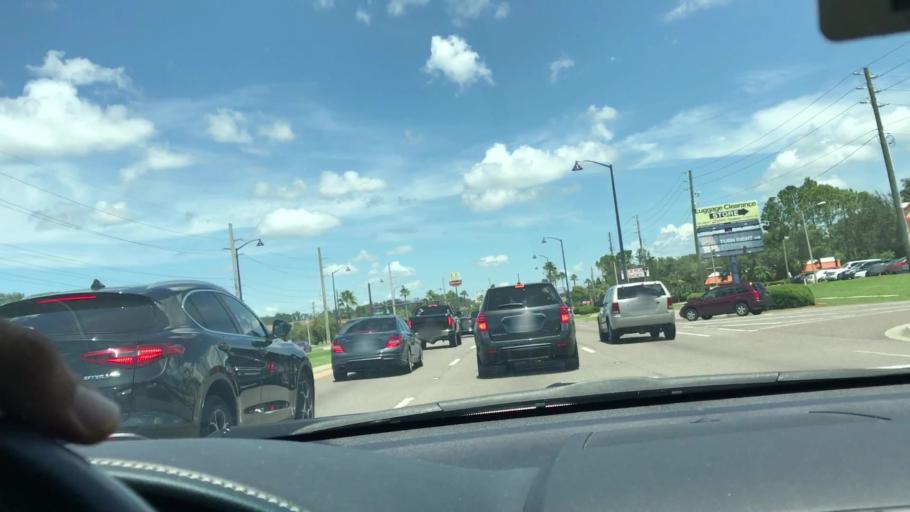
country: US
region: Florida
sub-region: Osceola County
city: Kissimmee
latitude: 28.3171
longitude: -81.4692
